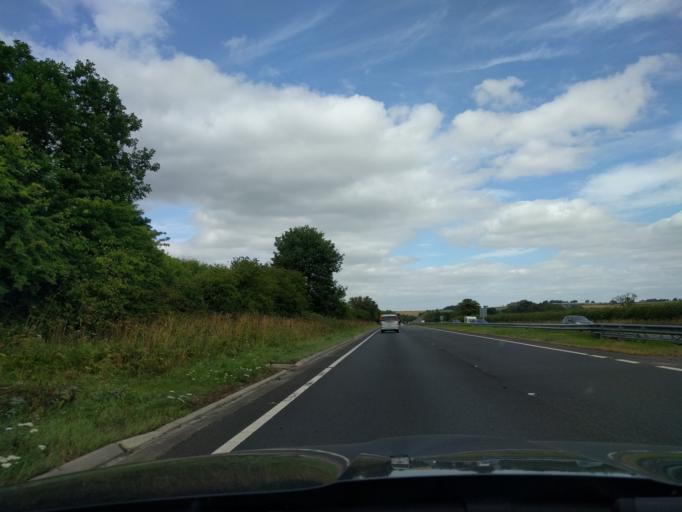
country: GB
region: England
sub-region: Northumberland
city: Felton
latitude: 55.3422
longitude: -1.7270
